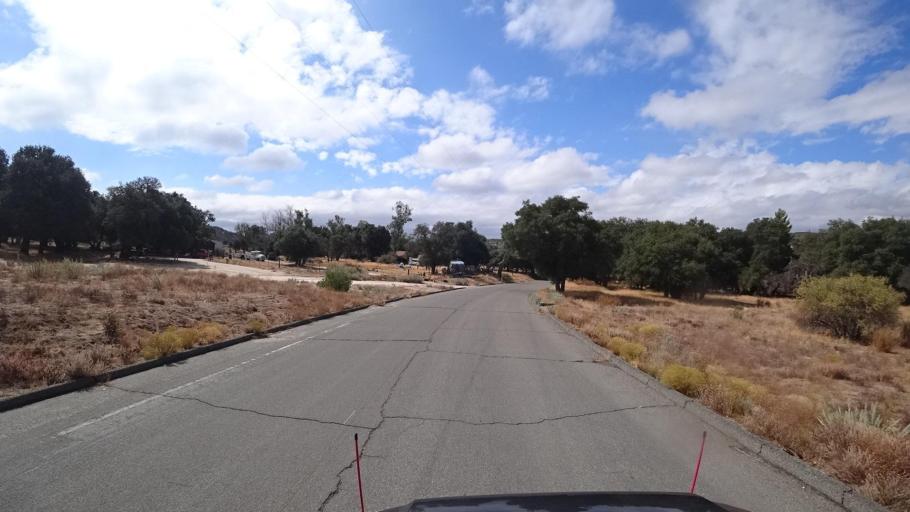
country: US
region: California
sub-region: San Diego County
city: Campo
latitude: 32.6936
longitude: -116.3323
